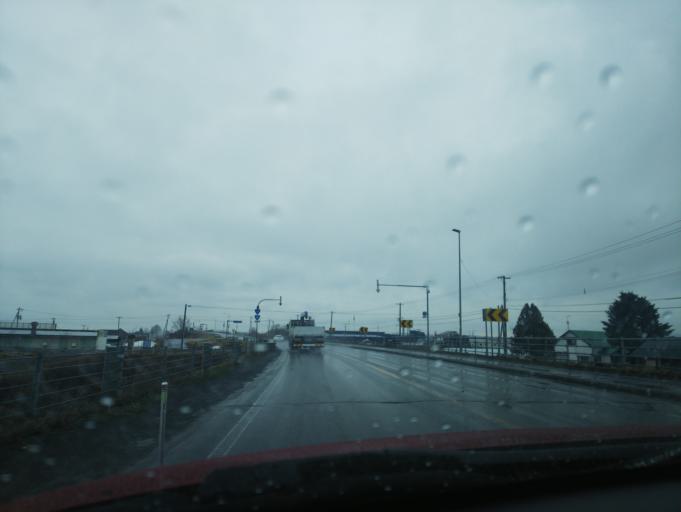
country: JP
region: Hokkaido
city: Nayoro
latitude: 44.1938
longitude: 142.3946
